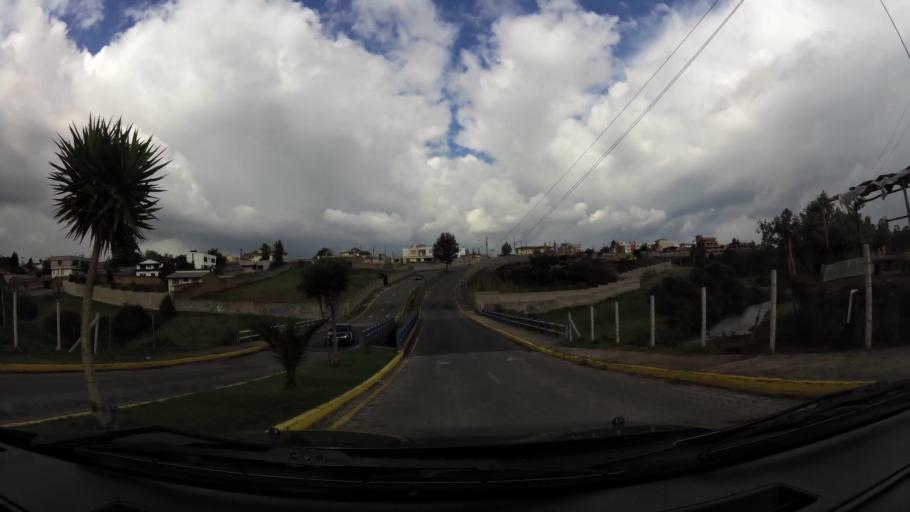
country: EC
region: Pichincha
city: Sangolqui
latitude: -0.3276
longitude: -78.4605
